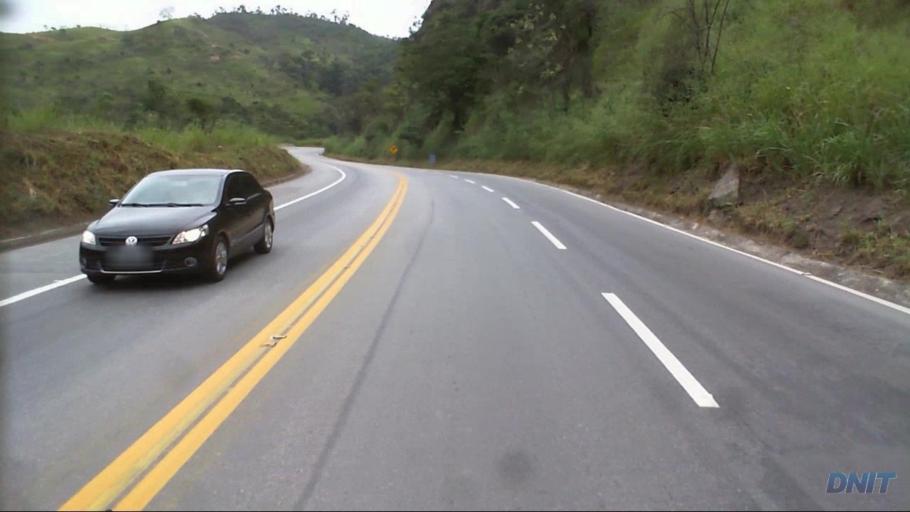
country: BR
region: Minas Gerais
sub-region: Timoteo
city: Timoteo
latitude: -19.6392
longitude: -42.8151
